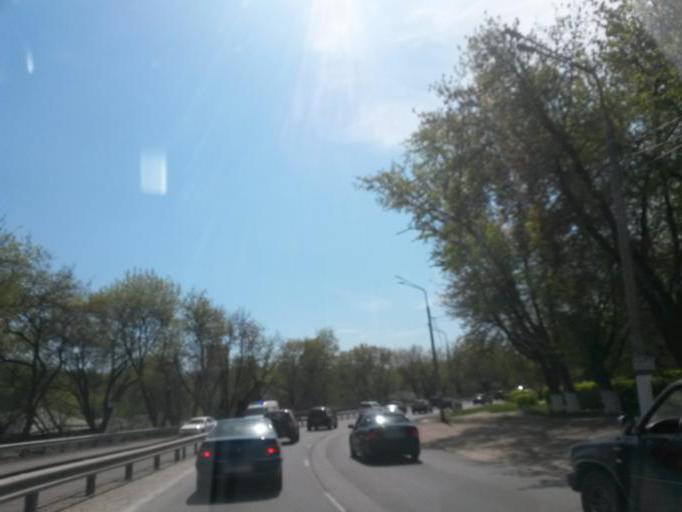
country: RU
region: Moskovskaya
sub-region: Podol'skiy Rayon
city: Podol'sk
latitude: 55.4396
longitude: 37.5566
